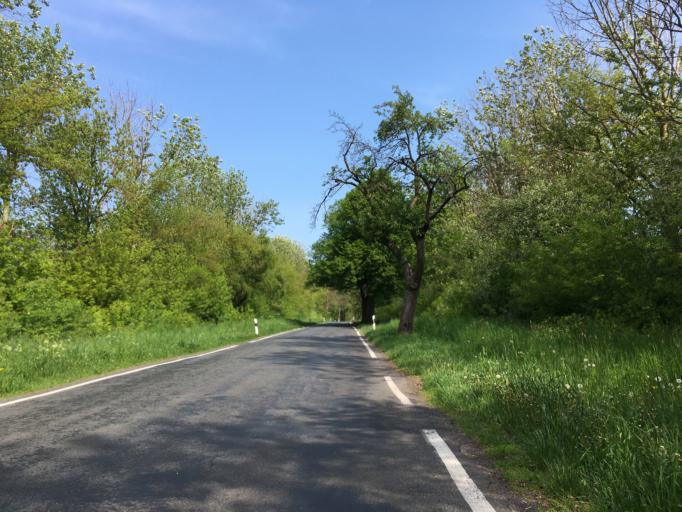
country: DE
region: Brandenburg
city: Werneuchen
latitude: 52.6634
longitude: 13.7316
